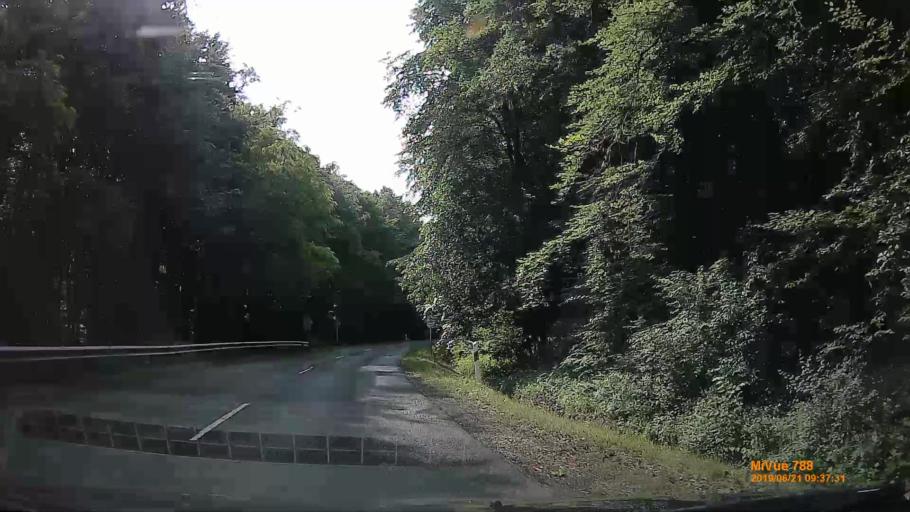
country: HU
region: Somogy
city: Taszar
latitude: 46.3147
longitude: 17.9175
